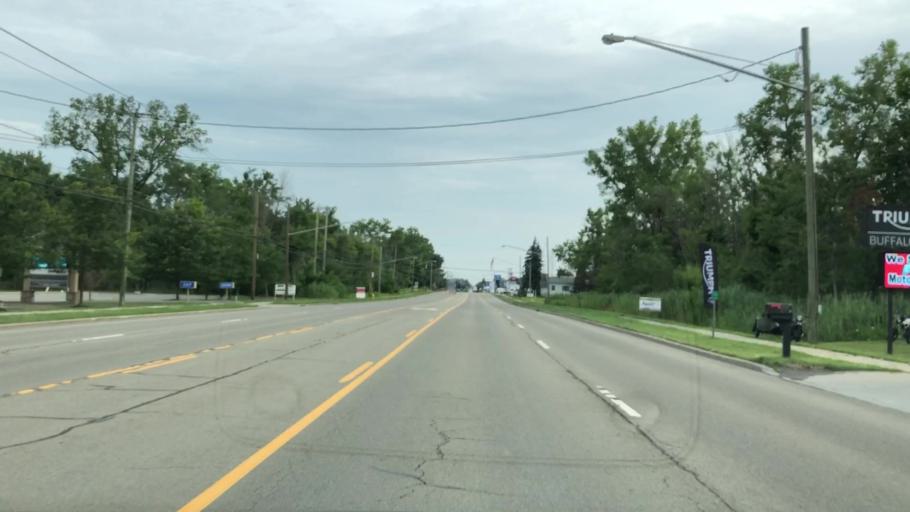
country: US
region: New York
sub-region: Erie County
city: Depew
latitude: 42.8860
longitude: -78.6969
